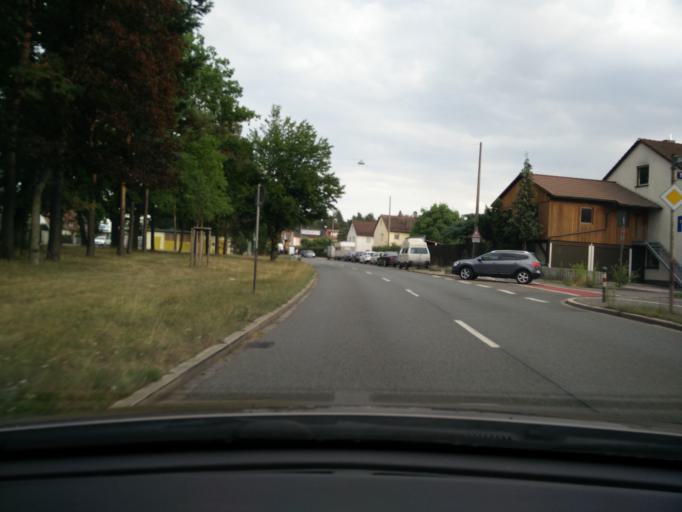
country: DE
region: Bavaria
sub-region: Regierungsbezirk Mittelfranken
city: Wendelstein
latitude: 49.3999
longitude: 11.1204
